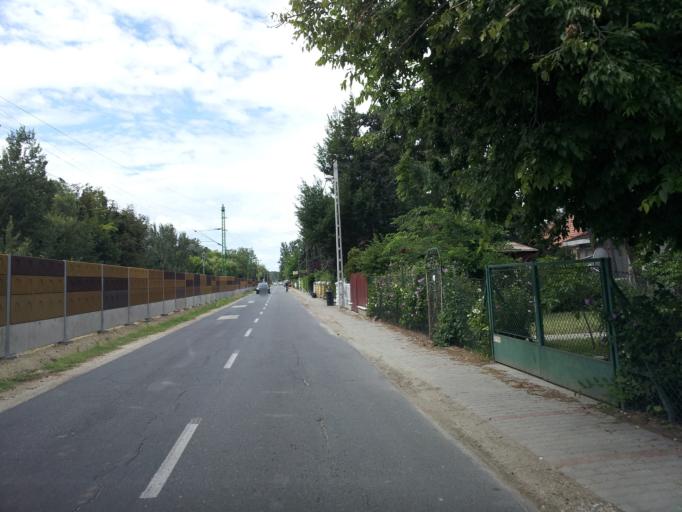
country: HU
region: Somogy
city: Balatonszabadi
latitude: 46.9315
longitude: 18.1136
